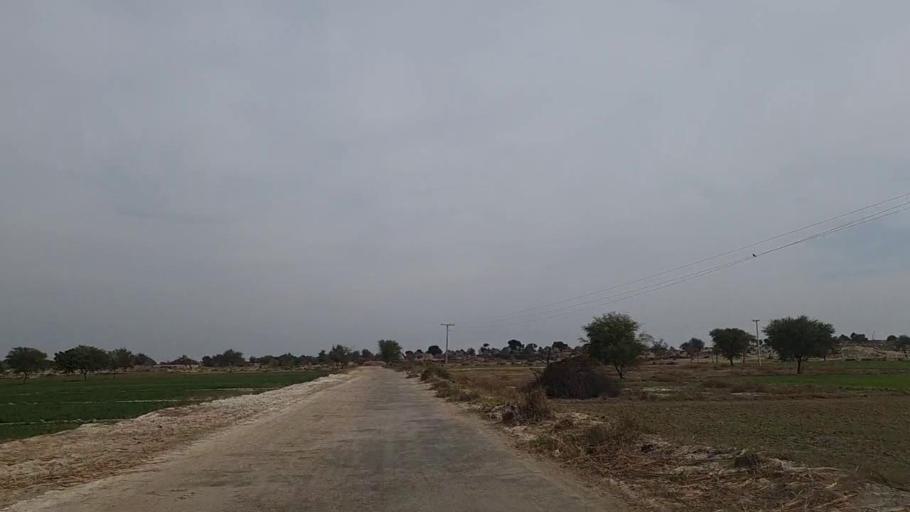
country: PK
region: Sindh
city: Jam Sahib
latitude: 26.4001
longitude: 68.5178
